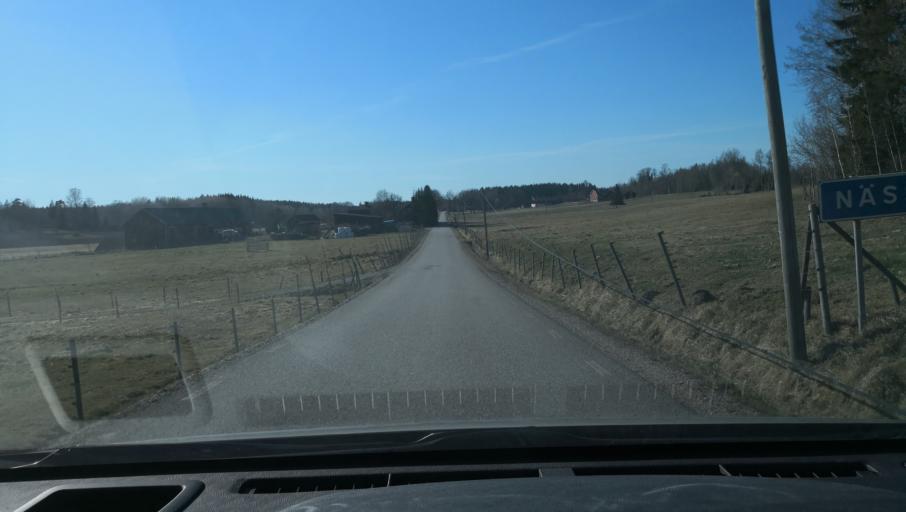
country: SE
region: Vaestmanland
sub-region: Sala Kommun
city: Sala
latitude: 60.0778
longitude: 16.4730
